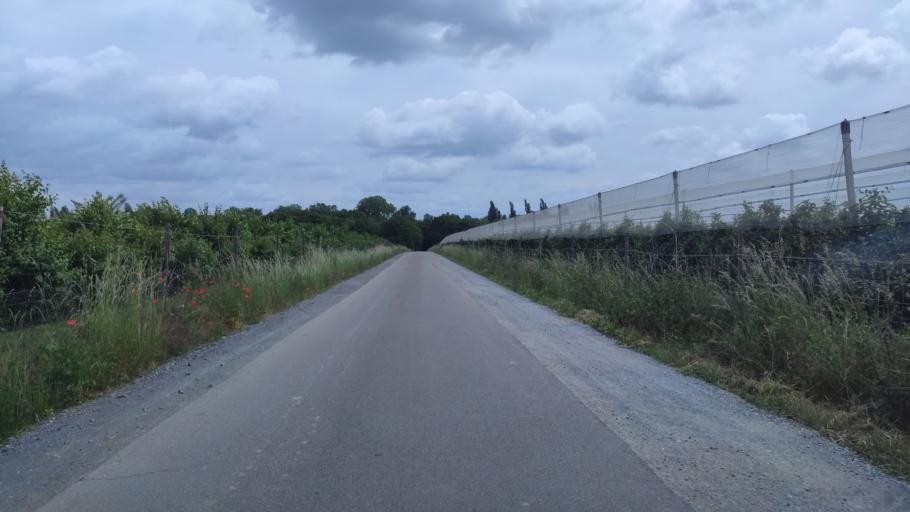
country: DE
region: North Rhine-Westphalia
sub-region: Regierungsbezirk Dusseldorf
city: Neubrueck
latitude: 51.1434
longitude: 6.6515
